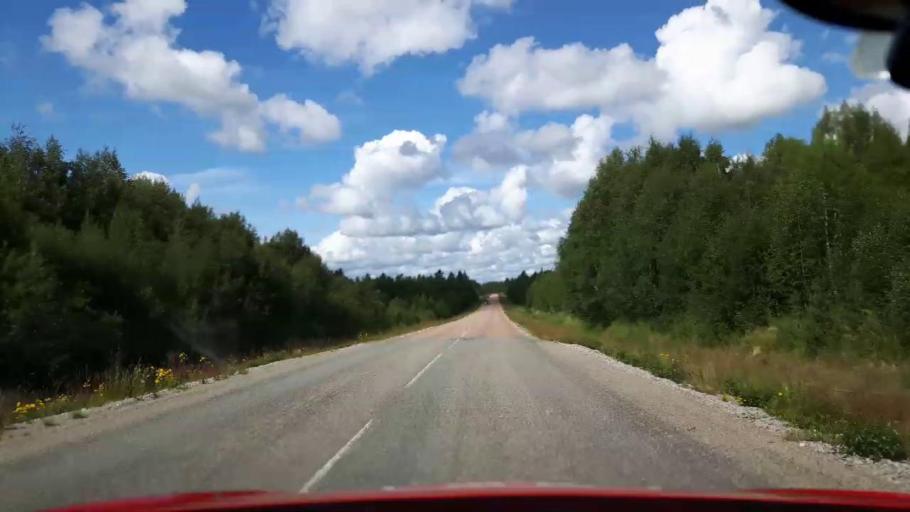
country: SE
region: Dalarna
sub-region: Alvdalens Kommun
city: AElvdalen
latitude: 61.8004
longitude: 13.6680
